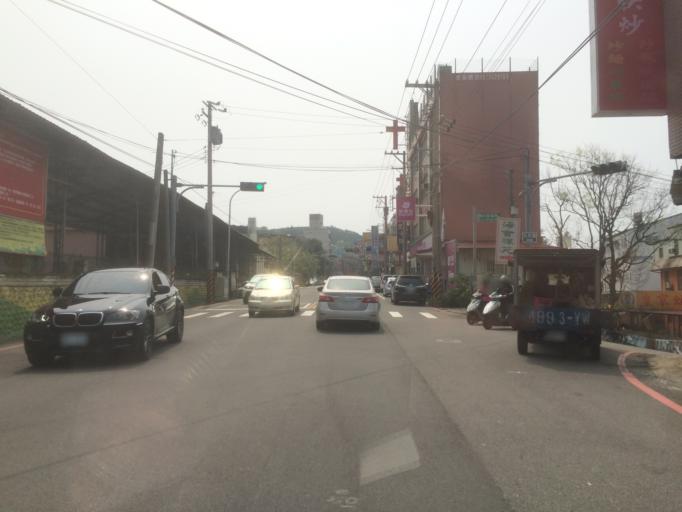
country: TW
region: Taiwan
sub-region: Hsinchu
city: Hsinchu
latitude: 24.7908
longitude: 120.9648
